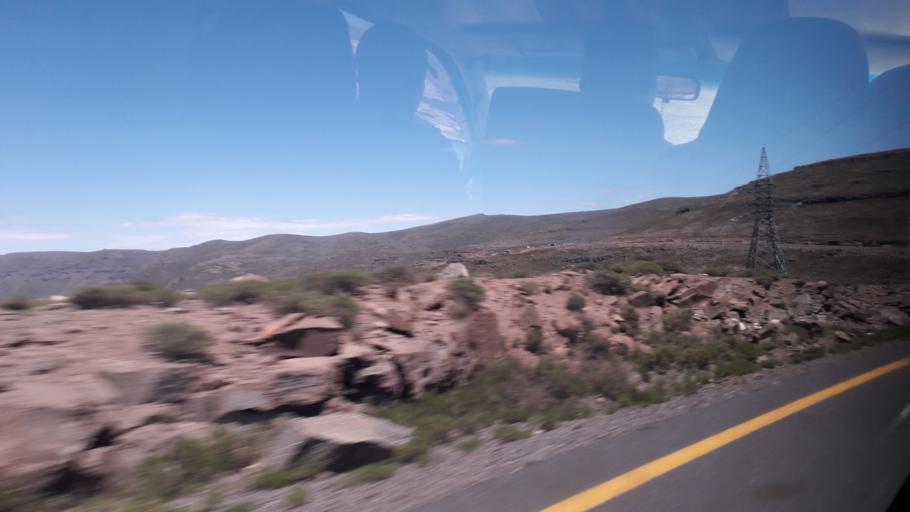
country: ZA
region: Orange Free State
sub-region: Thabo Mofutsanyana District Municipality
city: Phuthaditjhaba
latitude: -28.8335
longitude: 28.7405
